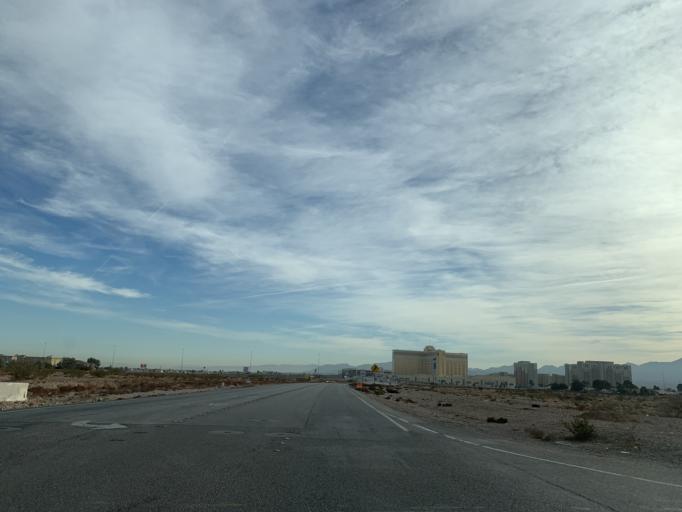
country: US
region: Nevada
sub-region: Clark County
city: Enterprise
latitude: 36.0135
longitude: -115.1899
